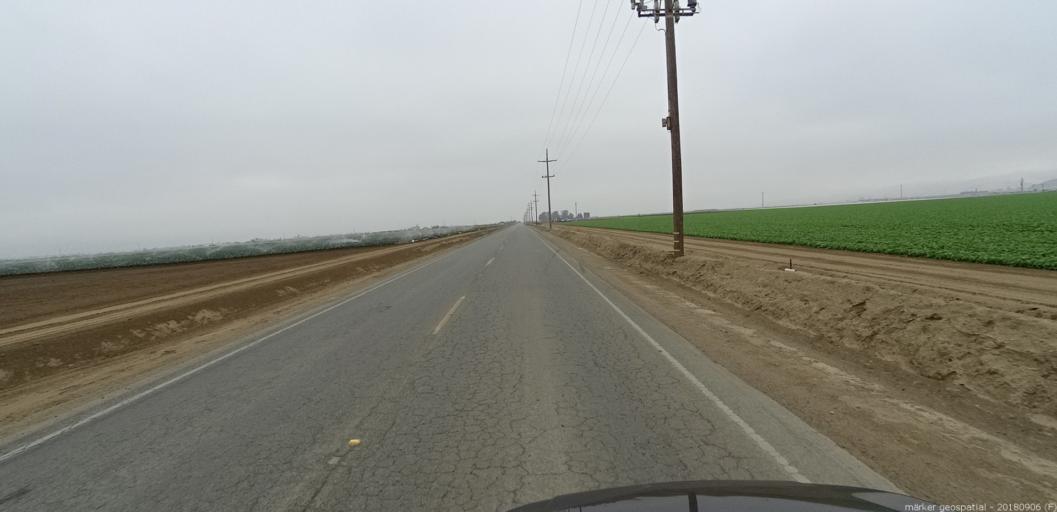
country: US
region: California
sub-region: Monterey County
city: Salinas
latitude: 36.6497
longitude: -121.5806
